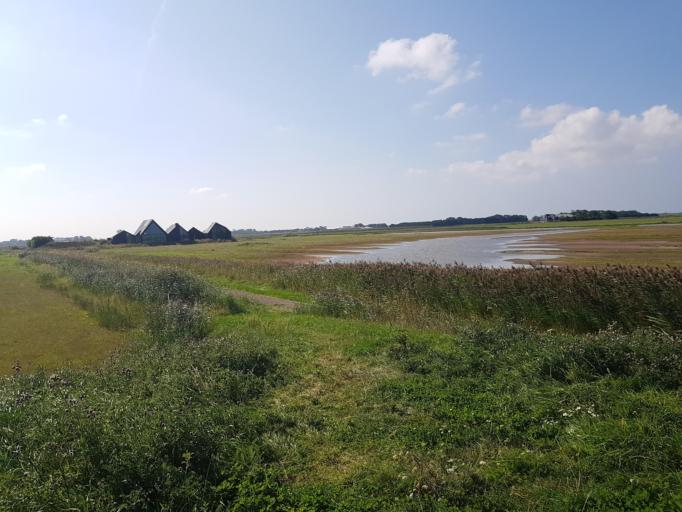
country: NL
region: North Holland
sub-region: Gemeente Texel
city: Den Burg
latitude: 53.1008
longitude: 4.8814
